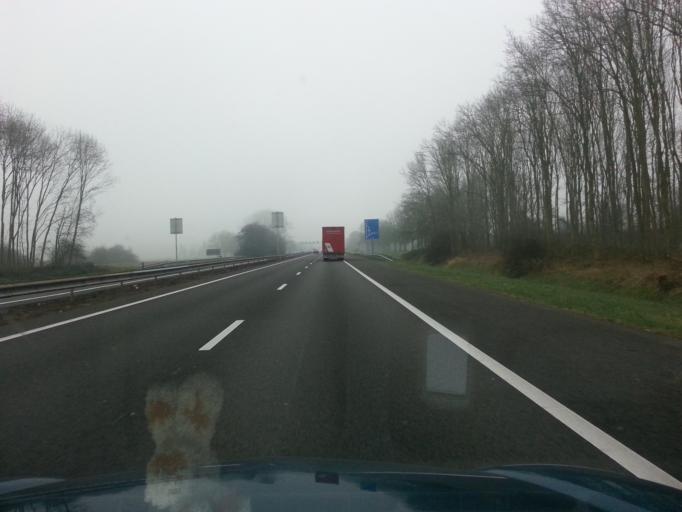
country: NL
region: Gelderland
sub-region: Gemeente Zevenaar
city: Zevenaar
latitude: 51.9137
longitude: 6.1414
